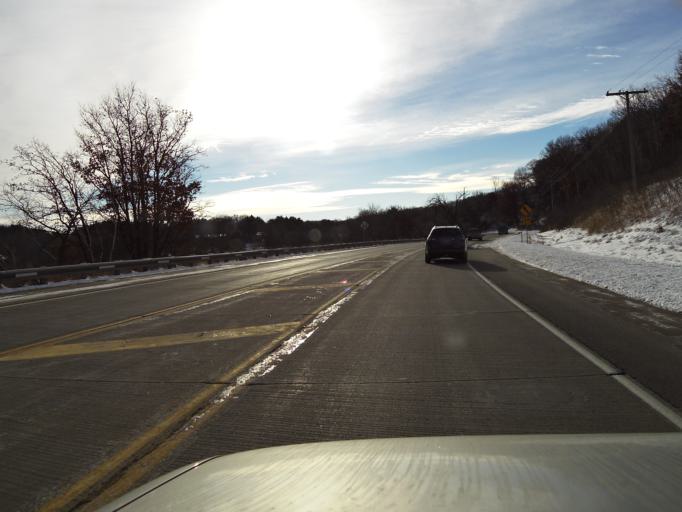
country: US
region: Minnesota
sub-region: Dakota County
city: Inver Grove Heights
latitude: 44.8280
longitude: -93.0844
